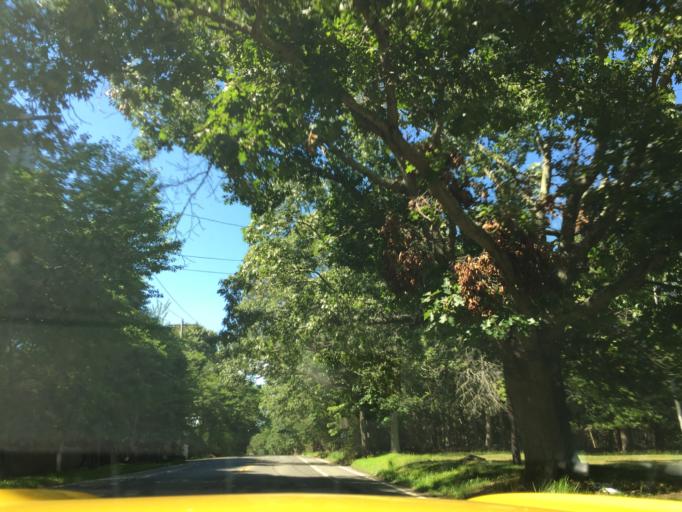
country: US
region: New York
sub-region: Suffolk County
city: Sag Harbor
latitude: 41.0343
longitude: -72.3136
